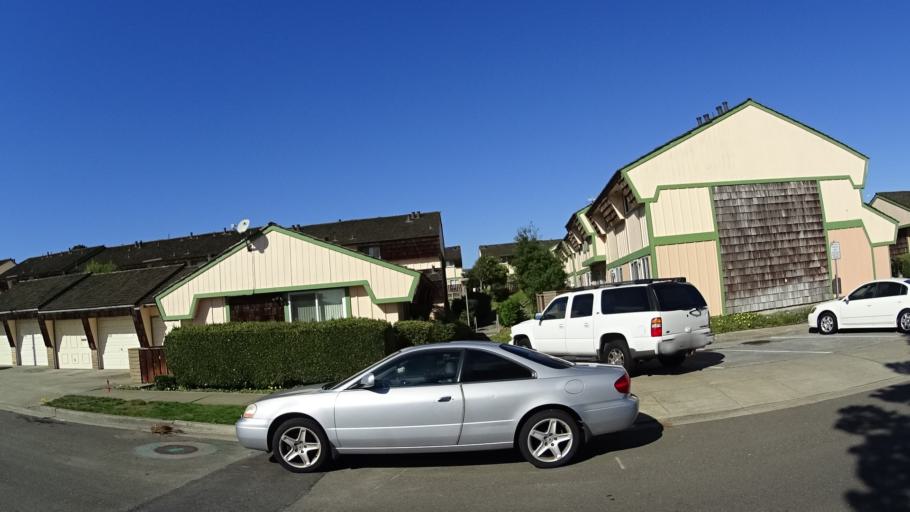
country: US
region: California
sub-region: San Mateo County
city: Colma
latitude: 37.6442
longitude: -122.4637
